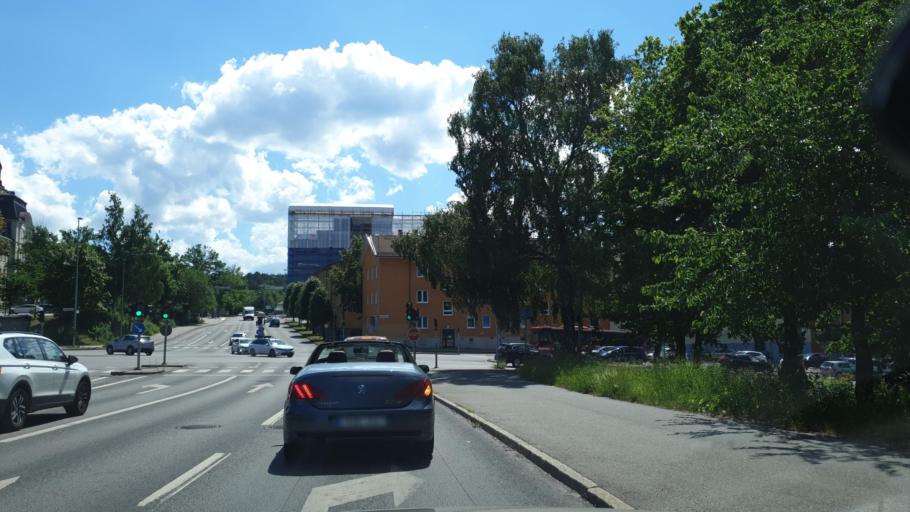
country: SE
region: Stockholm
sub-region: Sodertalje Kommun
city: Soedertaelje
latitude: 59.2014
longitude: 17.6324
